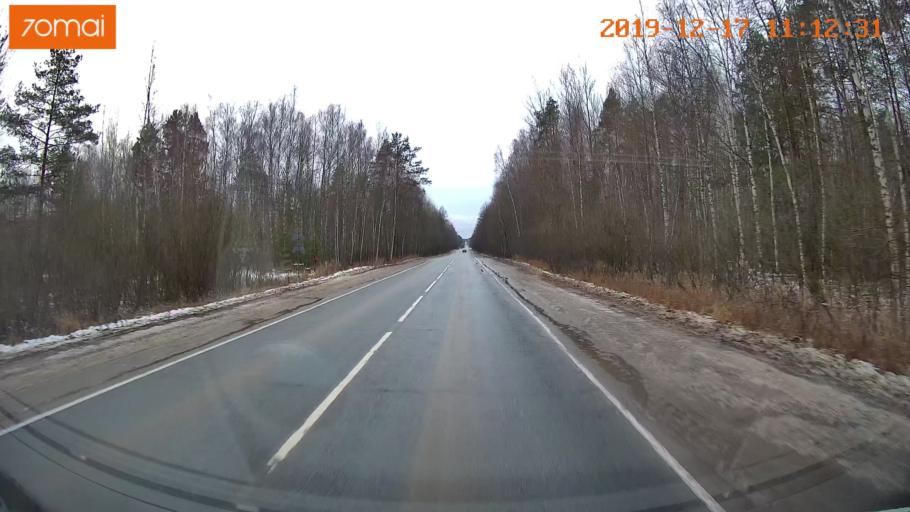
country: RU
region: Vladimir
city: Gus'-Khrustal'nyy
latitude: 55.5748
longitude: 40.6277
